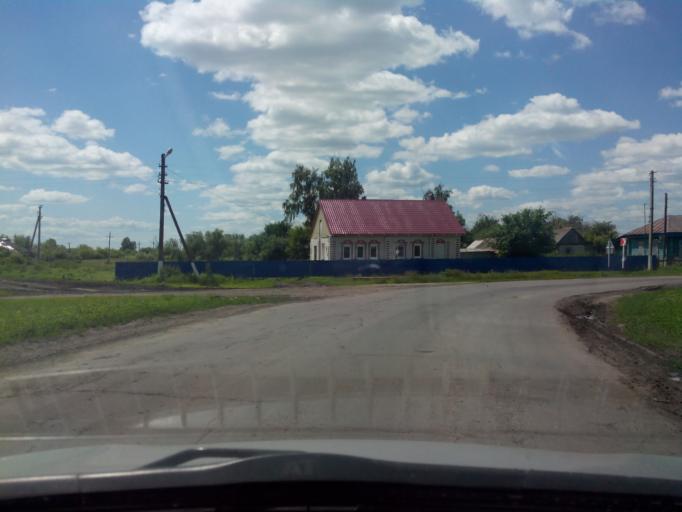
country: RU
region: Voronezj
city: Gribanovskiy
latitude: 51.6253
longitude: 41.9034
